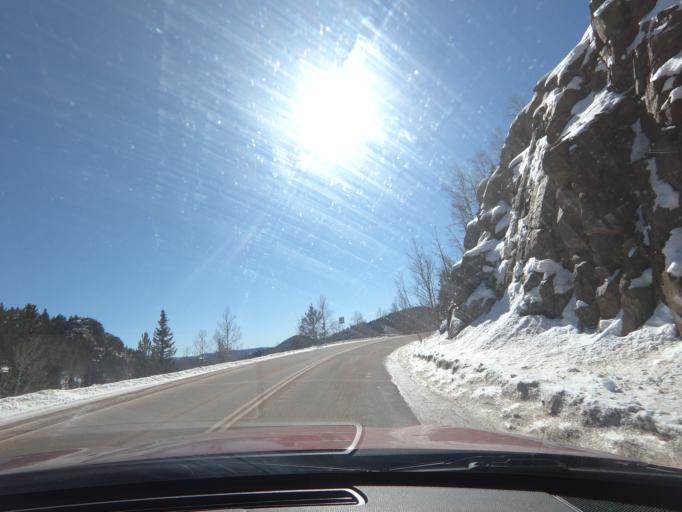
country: US
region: Colorado
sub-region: Teller County
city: Cripple Creek
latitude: 38.7479
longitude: -105.1003
